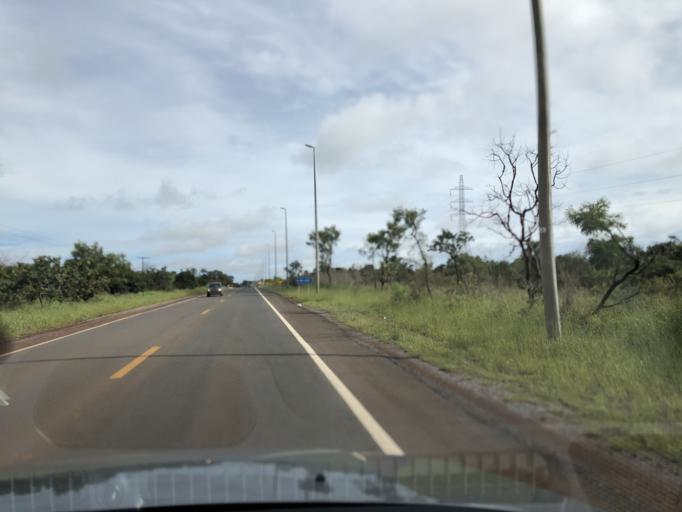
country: BR
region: Federal District
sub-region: Brasilia
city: Brasilia
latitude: -15.7001
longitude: -48.0883
